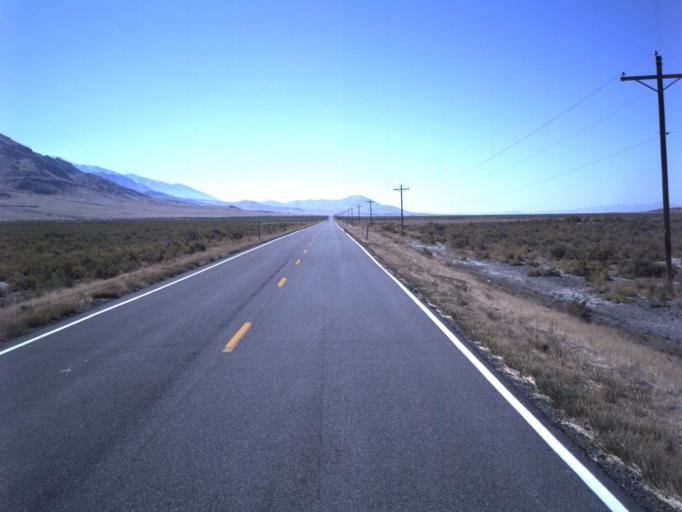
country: US
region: Utah
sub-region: Tooele County
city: Grantsville
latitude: 40.7309
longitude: -112.6574
